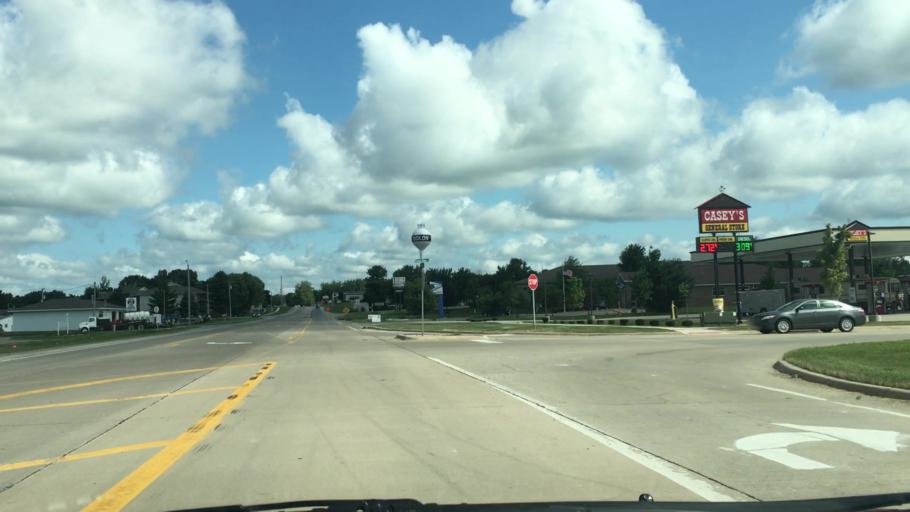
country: US
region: Iowa
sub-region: Johnson County
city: Solon
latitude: 41.7969
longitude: -91.4905
